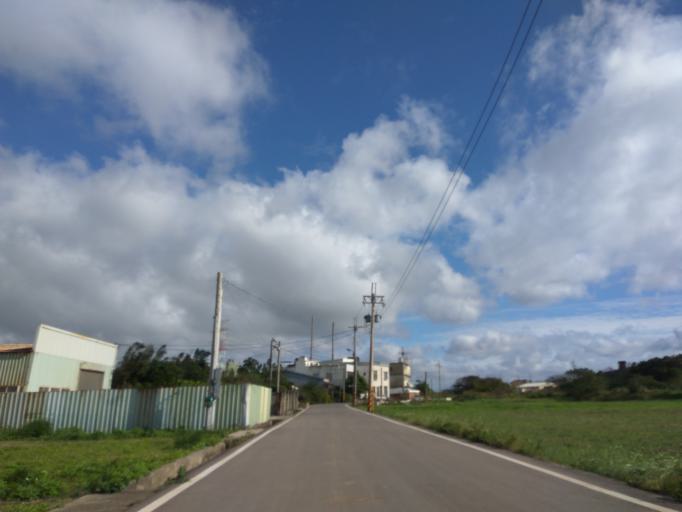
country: TW
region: Taiwan
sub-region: Hsinchu
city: Zhubei
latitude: 24.9727
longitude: 121.0707
